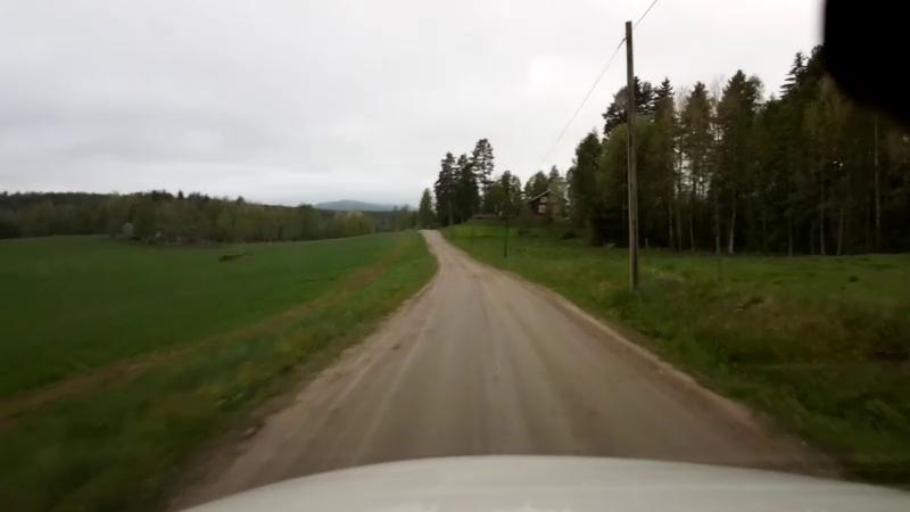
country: SE
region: Gaevleborg
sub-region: Ljusdals Kommun
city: Jaervsoe
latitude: 61.7741
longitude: 16.2034
